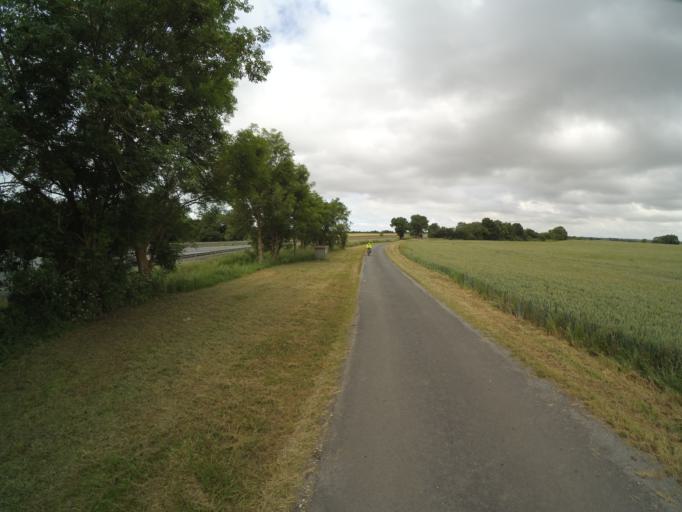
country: FR
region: Poitou-Charentes
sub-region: Departement de la Charente-Maritime
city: Saint-Laurent-de-la-Pree
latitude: 45.9963
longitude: -1.0400
